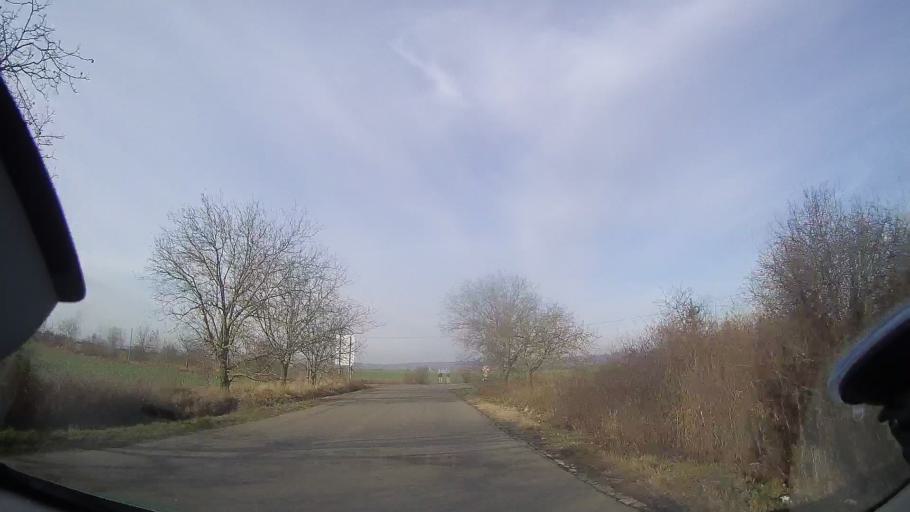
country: RO
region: Bihor
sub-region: Comuna Spinus
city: Spinus
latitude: 47.2264
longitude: 22.1674
